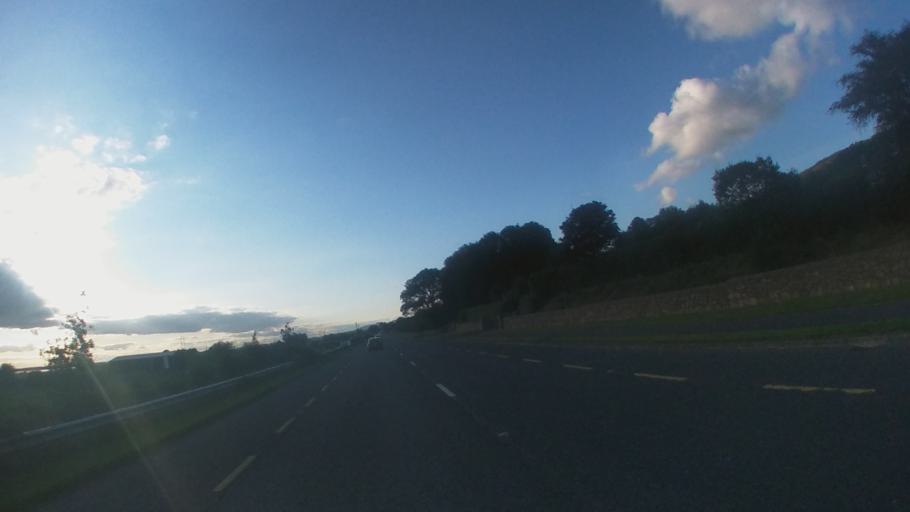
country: IE
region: Leinster
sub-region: Lu
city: Blackrock
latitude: 54.0038
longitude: -6.2819
